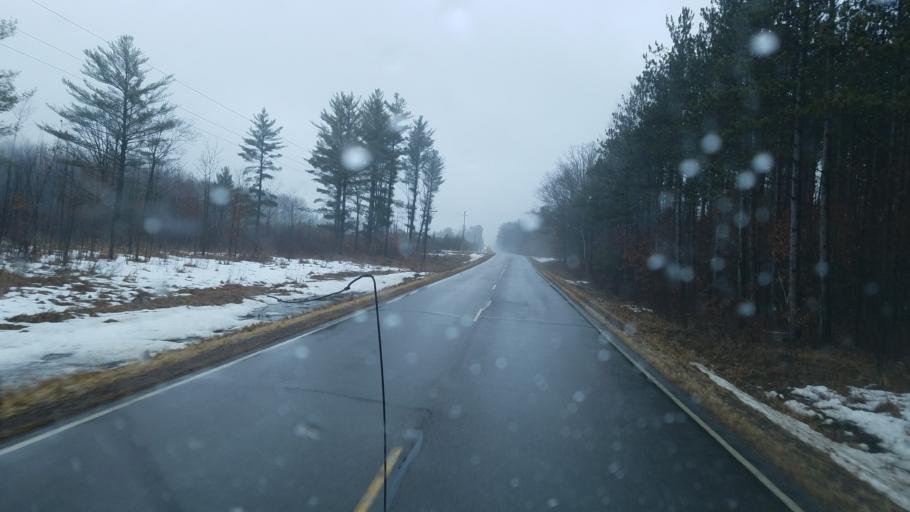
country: US
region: Wisconsin
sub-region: Wood County
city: Marshfield
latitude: 44.4953
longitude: -90.2797
